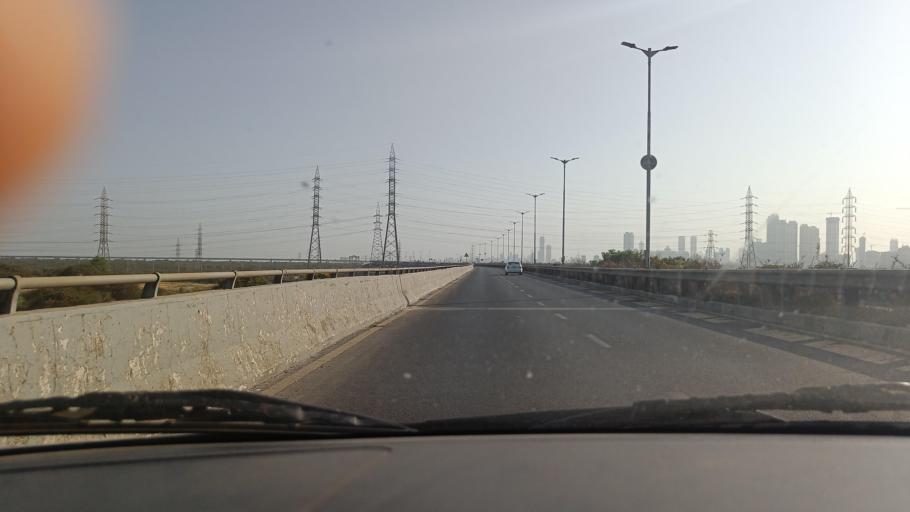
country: IN
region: Maharashtra
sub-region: Mumbai Suburban
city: Mumbai
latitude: 19.0187
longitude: 72.8739
